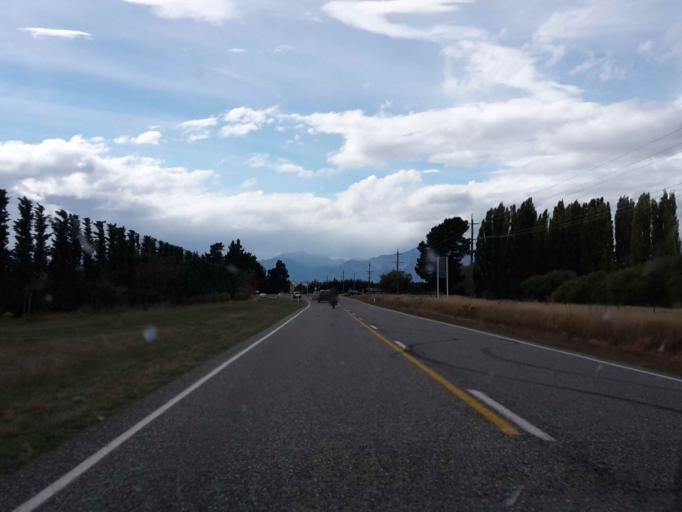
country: NZ
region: Otago
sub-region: Queenstown-Lakes District
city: Wanaka
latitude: -44.7364
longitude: 169.1340
